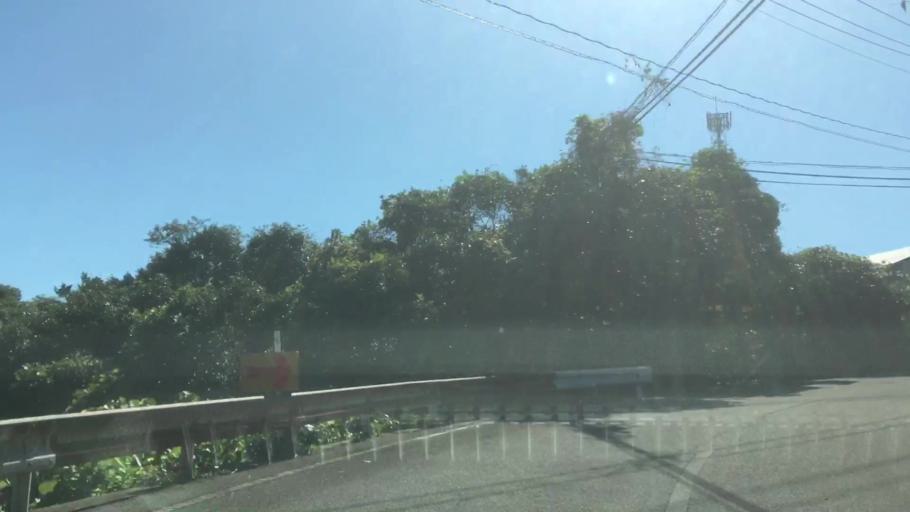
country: JP
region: Nagasaki
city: Sasebo
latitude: 33.0203
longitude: 129.5750
